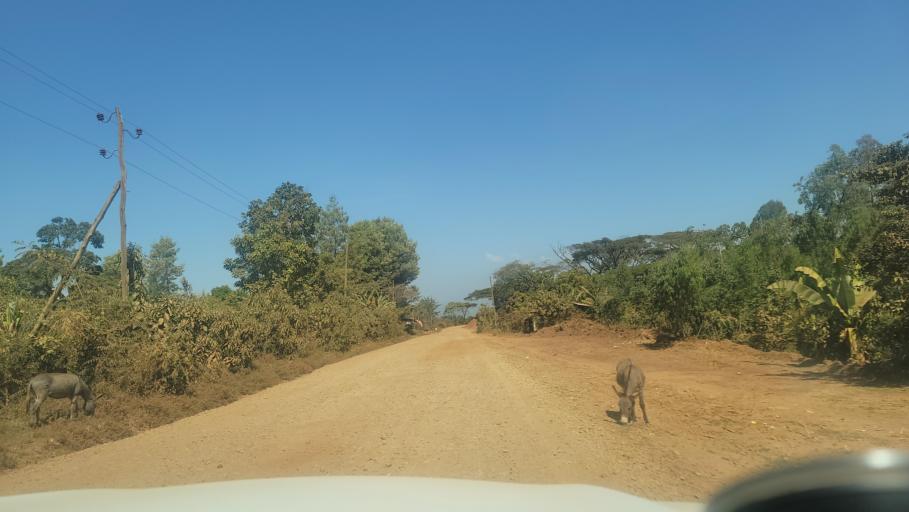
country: ET
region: Oromiya
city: Agaro
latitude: 7.8228
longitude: 36.5301
